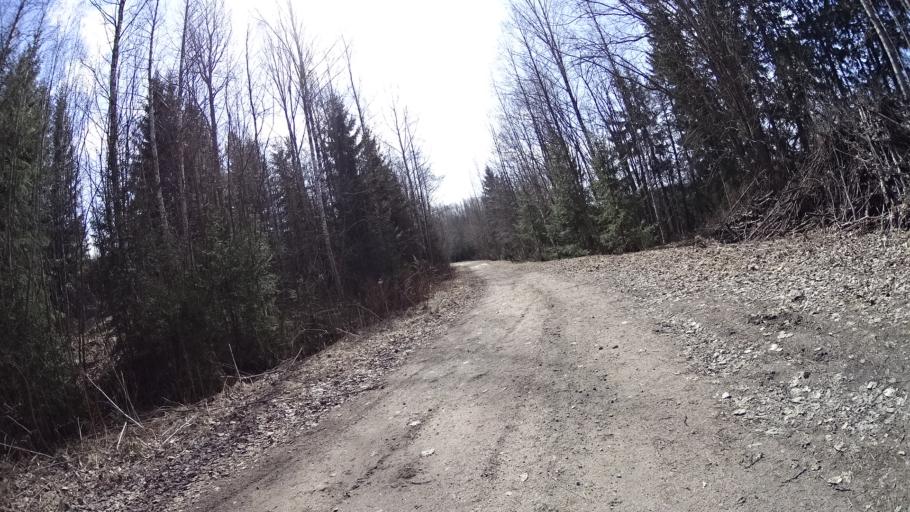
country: FI
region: Uusimaa
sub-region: Helsinki
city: Kilo
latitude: 60.3220
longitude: 24.8232
